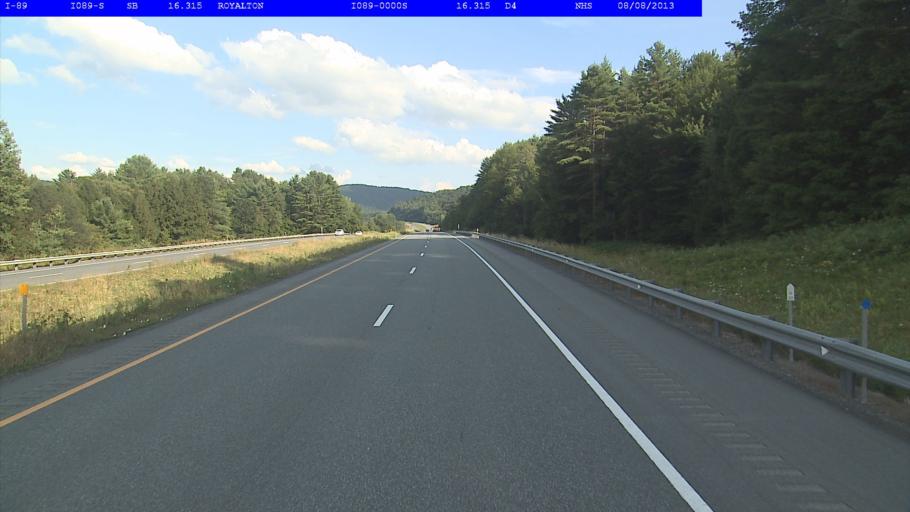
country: US
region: Vermont
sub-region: Windsor County
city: Woodstock
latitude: 43.7933
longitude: -72.5042
